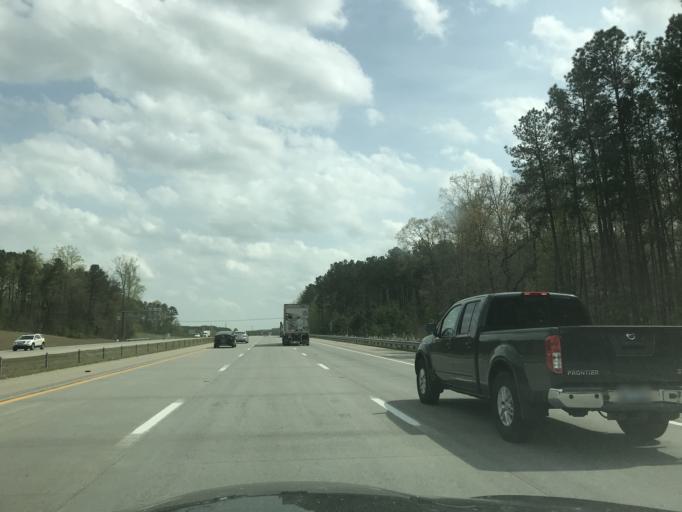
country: US
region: North Carolina
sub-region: Wake County
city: Knightdale
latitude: 35.7795
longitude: -78.5109
